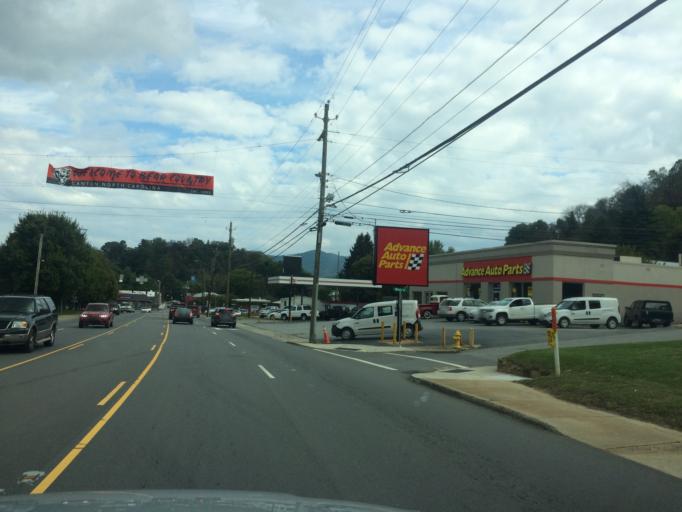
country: US
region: North Carolina
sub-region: Haywood County
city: Canton
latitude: 35.5312
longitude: -82.8470
